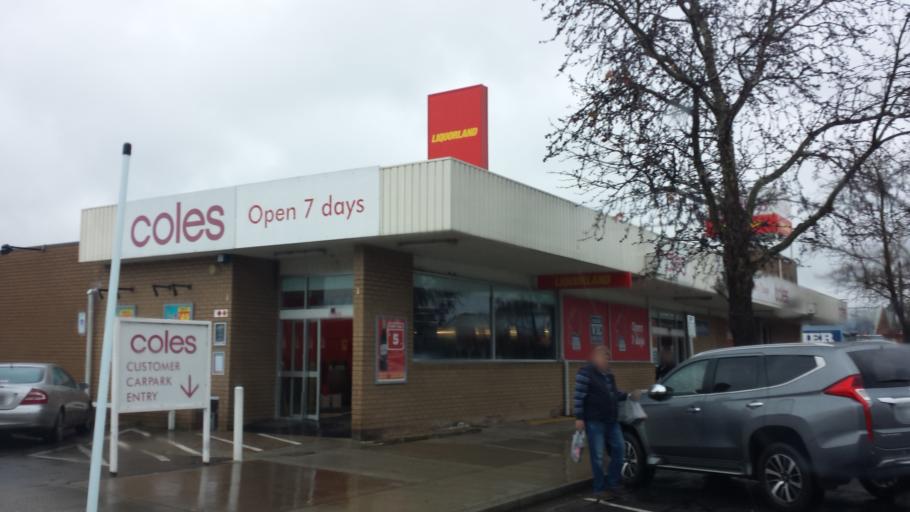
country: AU
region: Victoria
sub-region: Benalla
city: Benalla
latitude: -36.5496
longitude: 145.9853
